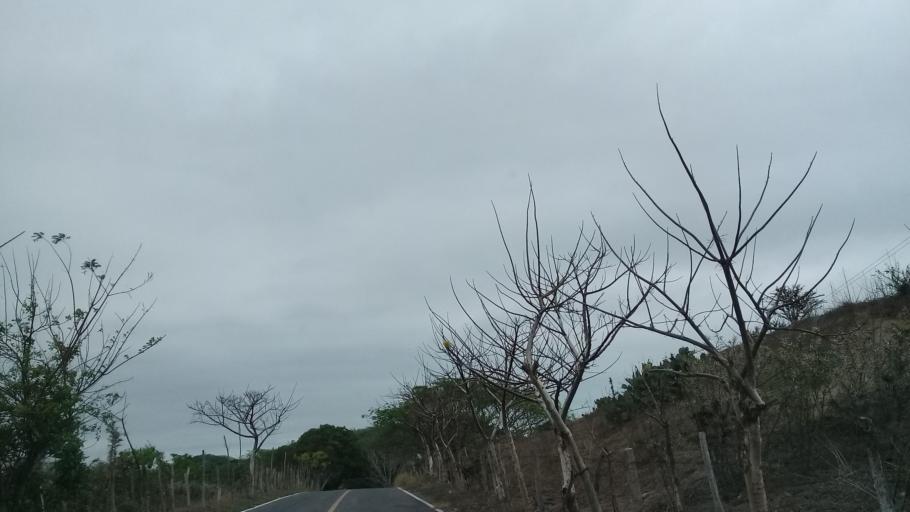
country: MX
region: Veracruz
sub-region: La Antigua
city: Nicolas Blanco (San Pancho)
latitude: 19.3352
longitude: -96.3266
